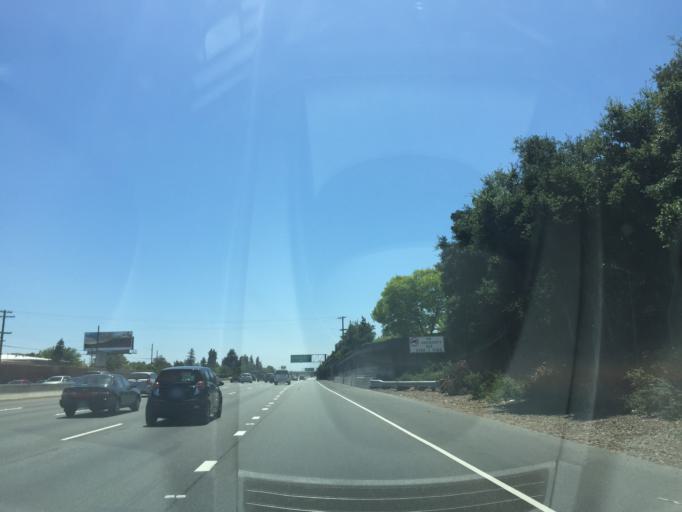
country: US
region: California
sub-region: San Mateo County
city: East Palo Alto
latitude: 37.4650
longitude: -122.1490
